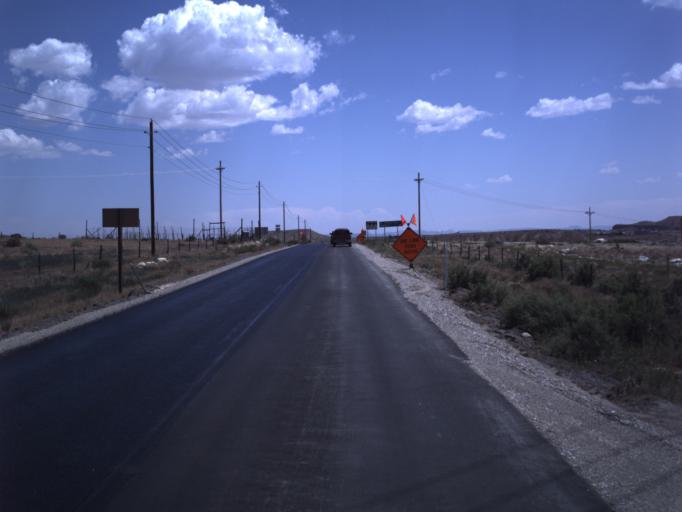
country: US
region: Utah
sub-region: Emery County
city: Orangeville
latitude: 39.2562
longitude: -111.1004
